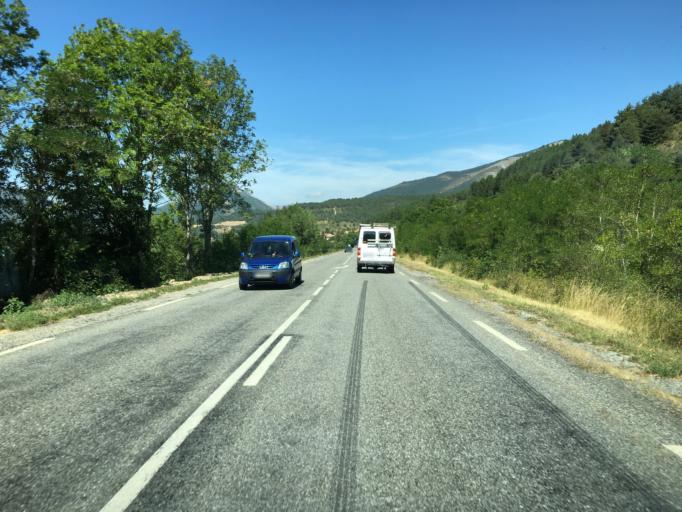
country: FR
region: Provence-Alpes-Cote d'Azur
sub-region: Departement des Hautes-Alpes
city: Veynes
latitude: 44.5617
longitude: 5.7638
